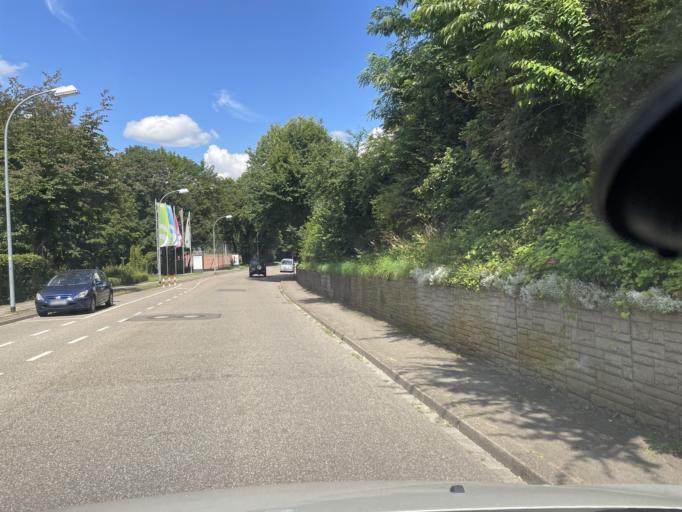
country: DE
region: Saarland
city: Saarbrucken
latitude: 49.2436
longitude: 7.0168
